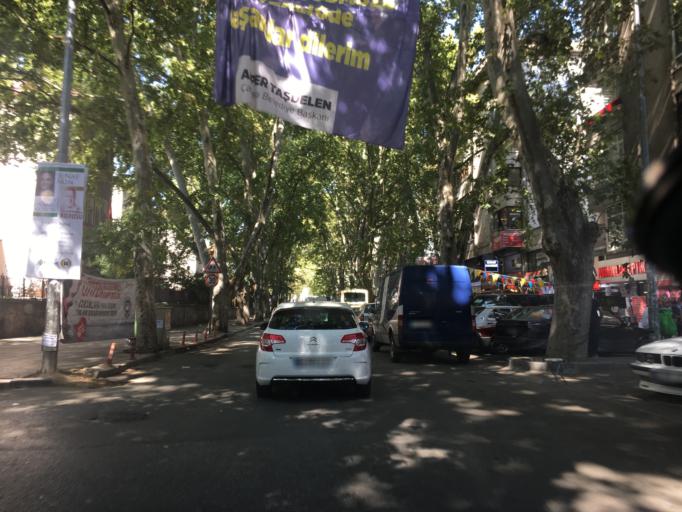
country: TR
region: Ankara
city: Ankara
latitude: 39.9200
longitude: 32.8506
